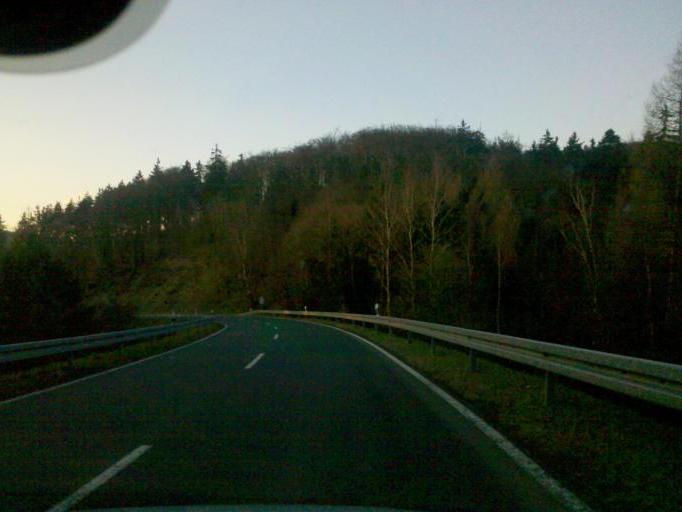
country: DE
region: Hesse
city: Dillenburg
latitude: 50.7966
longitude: 8.2675
